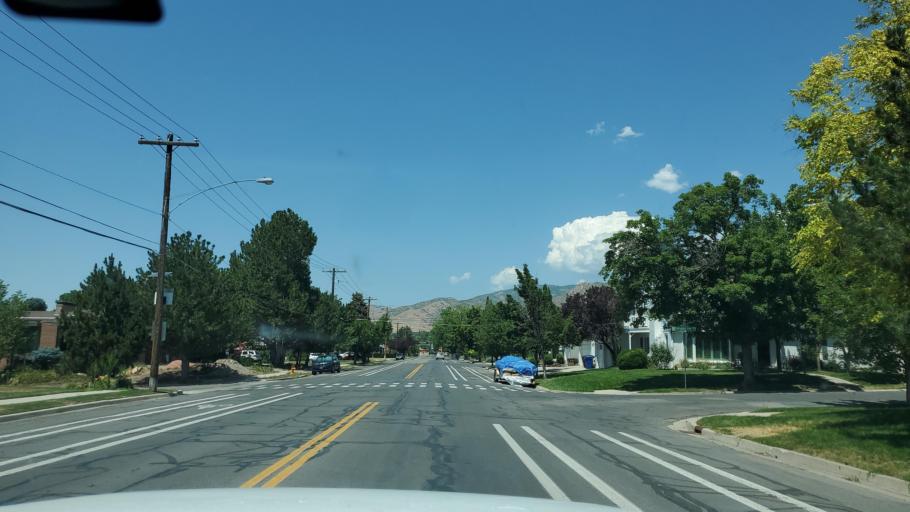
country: US
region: Utah
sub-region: Salt Lake County
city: Canyon Rim
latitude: 40.7208
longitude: -111.8245
